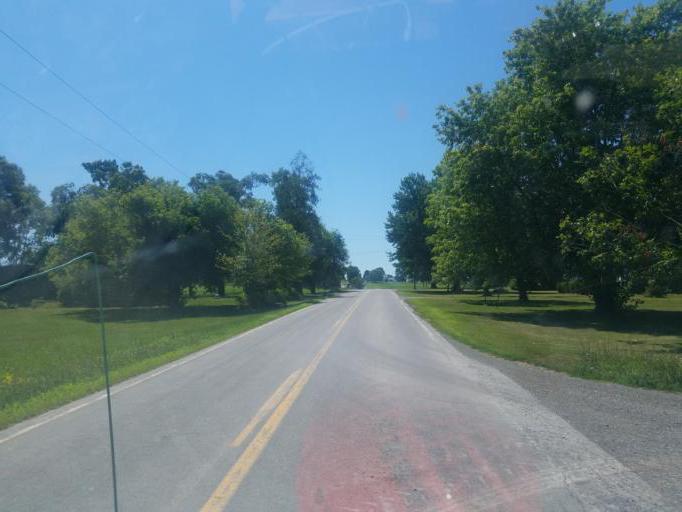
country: US
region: New York
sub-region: Ontario County
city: Geneva
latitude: 42.7991
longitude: -77.0168
